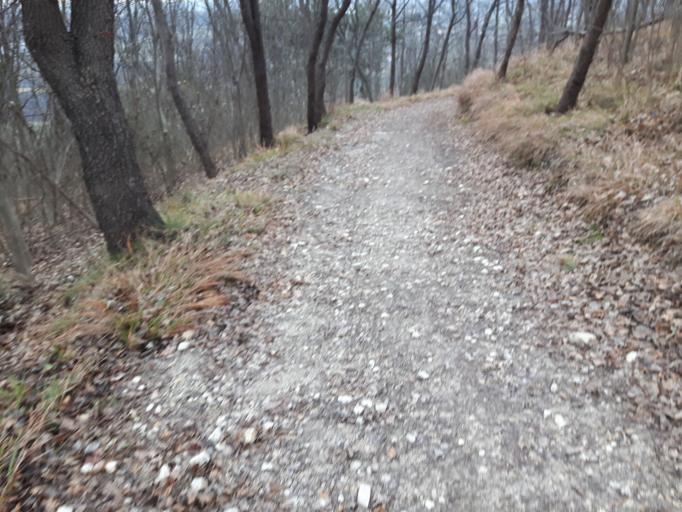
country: IT
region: Veneto
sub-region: Provincia di Padova
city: Arqua Petrarca
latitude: 45.2750
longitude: 11.7409
